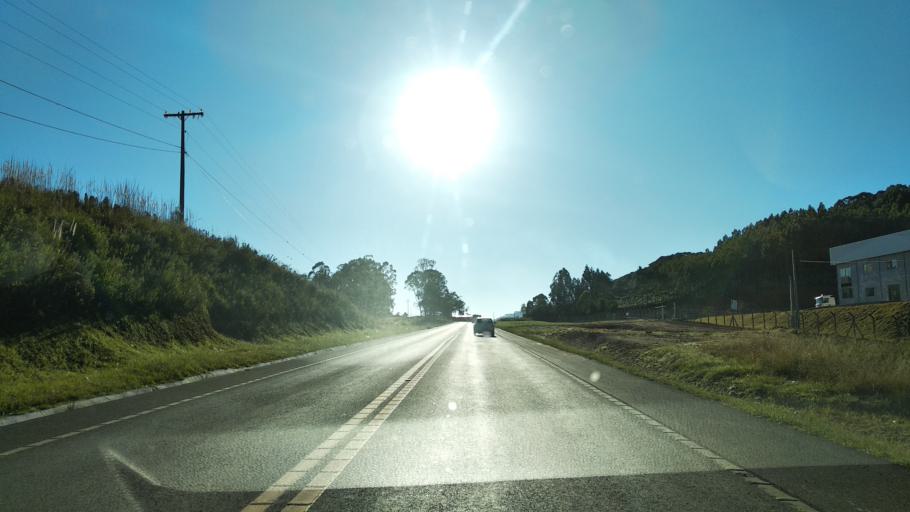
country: BR
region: Santa Catarina
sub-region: Lages
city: Lages
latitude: -27.7937
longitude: -50.3781
